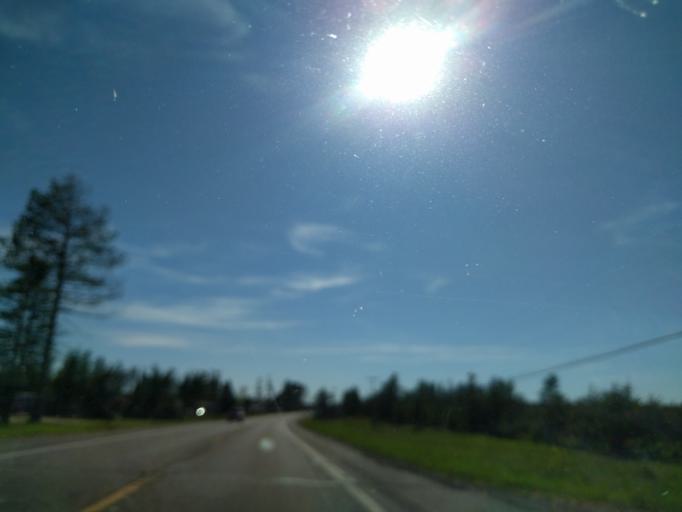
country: US
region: Michigan
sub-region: Marquette County
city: Gwinn
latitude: 46.2766
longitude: -87.3980
